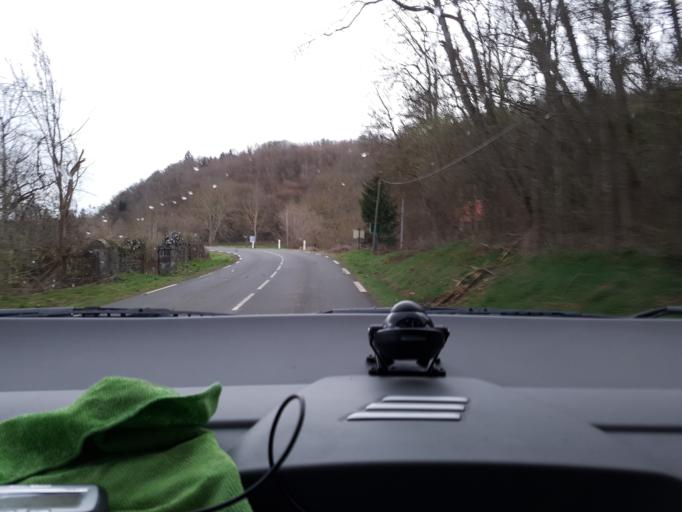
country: FR
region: Auvergne
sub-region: Departement du Puy-de-Dome
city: Saint-Ours
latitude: 45.8293
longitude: 2.8442
